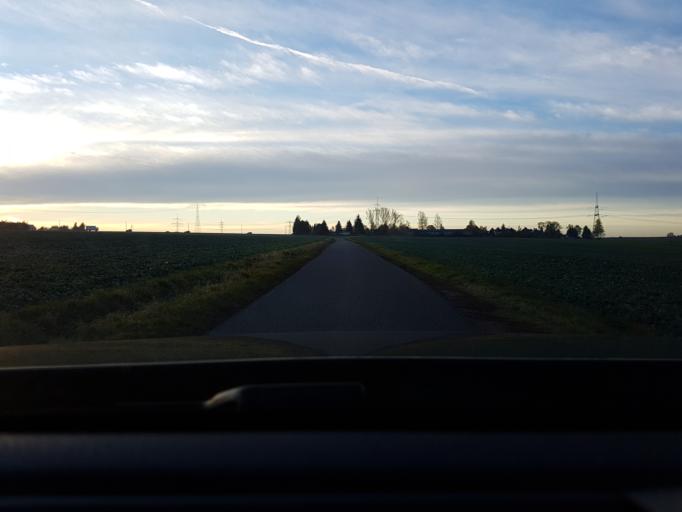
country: DE
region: Saxony
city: Altmittweida
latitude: 50.9565
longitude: 12.9691
